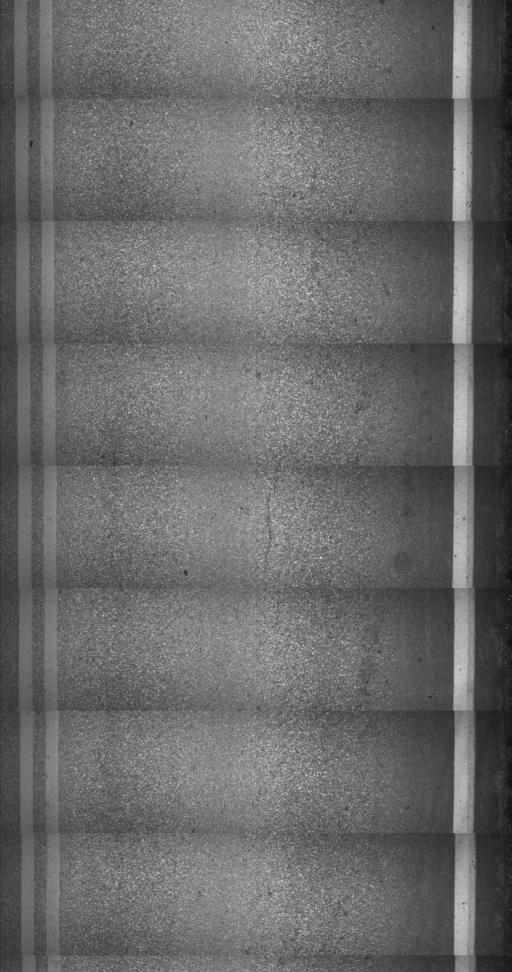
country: US
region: Vermont
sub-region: Rutland County
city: Poultney
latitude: 43.5240
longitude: -73.2318
